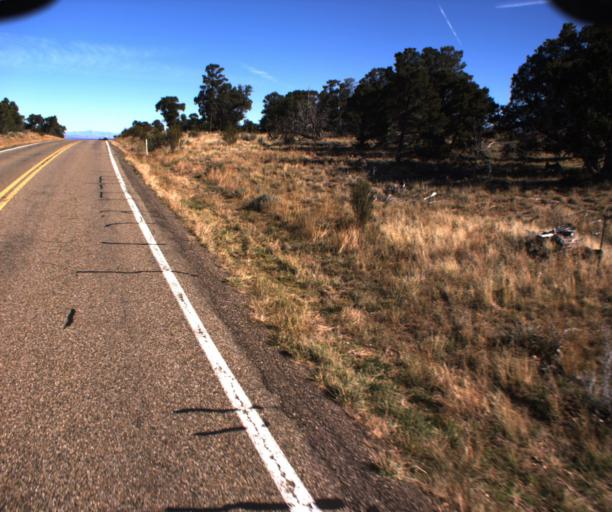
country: US
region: Arizona
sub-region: Coconino County
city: Fredonia
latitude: 36.8113
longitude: -112.2548
